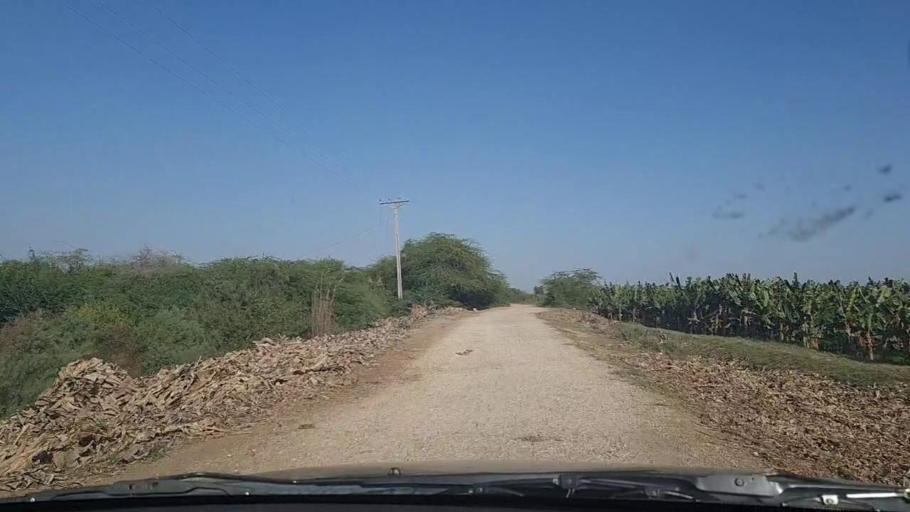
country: PK
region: Sindh
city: Chuhar Jamali
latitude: 24.3237
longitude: 67.7574
